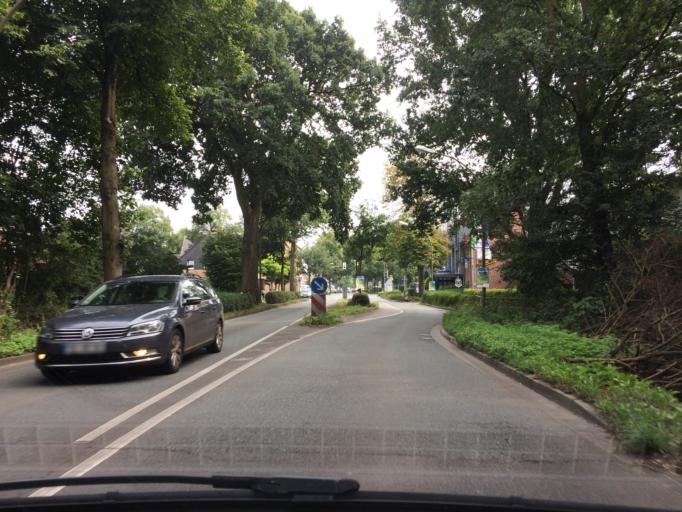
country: DE
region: North Rhine-Westphalia
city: Dorsten
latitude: 51.6854
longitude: 6.9525
